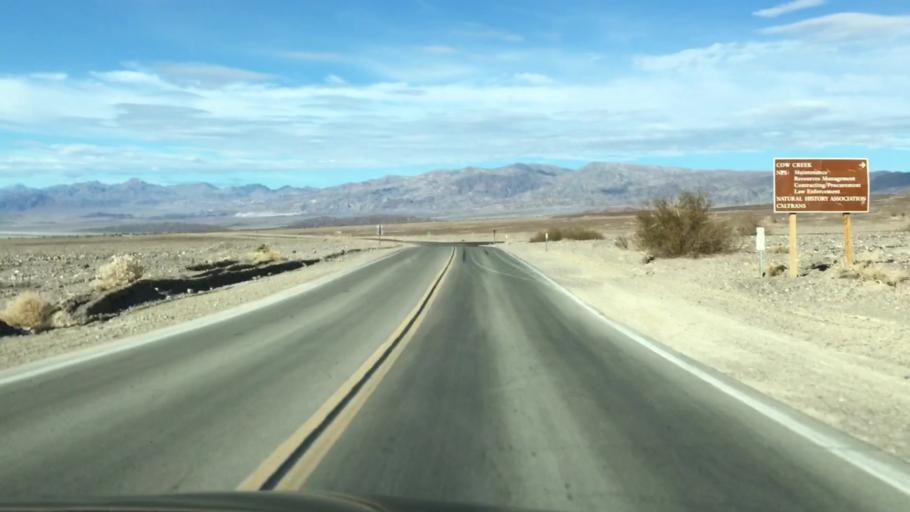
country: US
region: Nevada
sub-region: Nye County
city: Beatty
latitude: 36.5003
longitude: -116.8755
